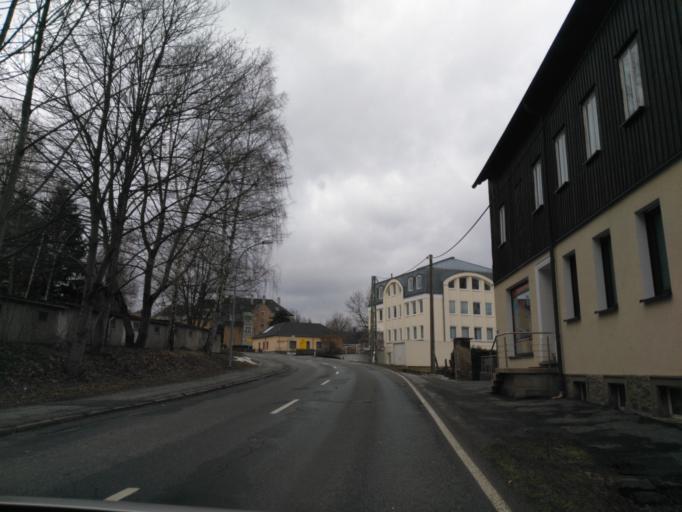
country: DE
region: Saxony
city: Annaberg-Buchholz
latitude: 50.5856
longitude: 13.0188
